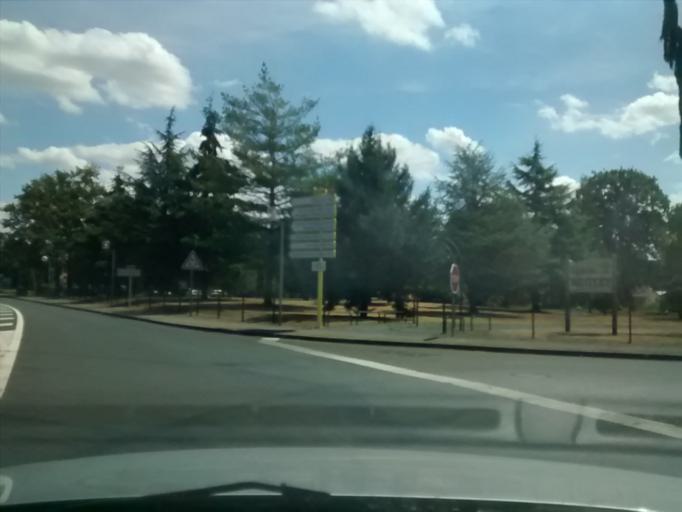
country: FR
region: Pays de la Loire
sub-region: Departement de la Sarthe
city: Mulsanne
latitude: 47.9132
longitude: 0.2453
